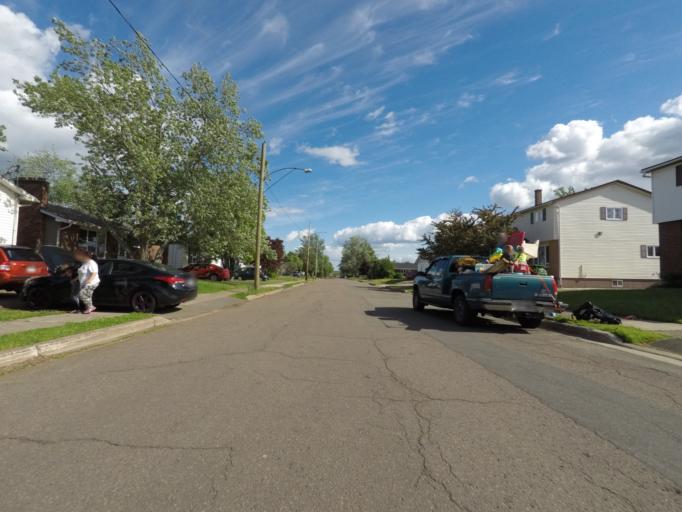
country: CA
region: New Brunswick
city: Moncton
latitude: 46.1003
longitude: -64.8264
